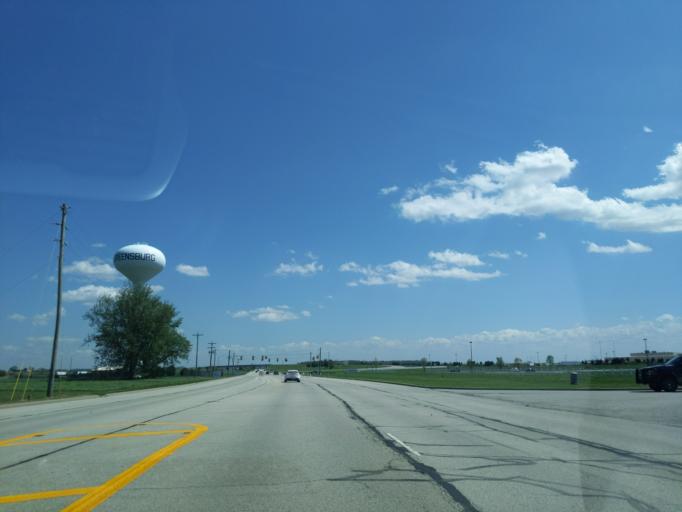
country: US
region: Indiana
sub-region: Decatur County
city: Greensburg
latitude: 39.3802
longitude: -85.5428
